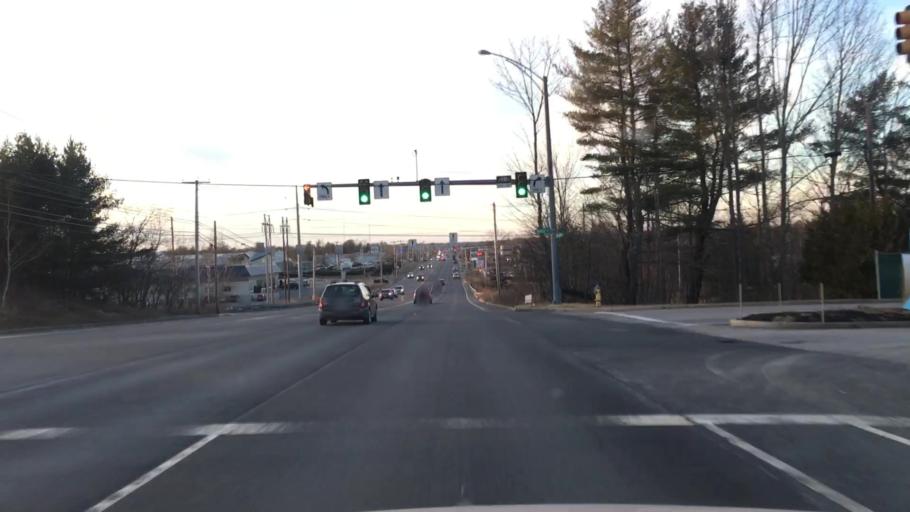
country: US
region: Maine
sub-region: Penobscot County
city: Brewer
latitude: 44.7739
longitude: -68.7274
